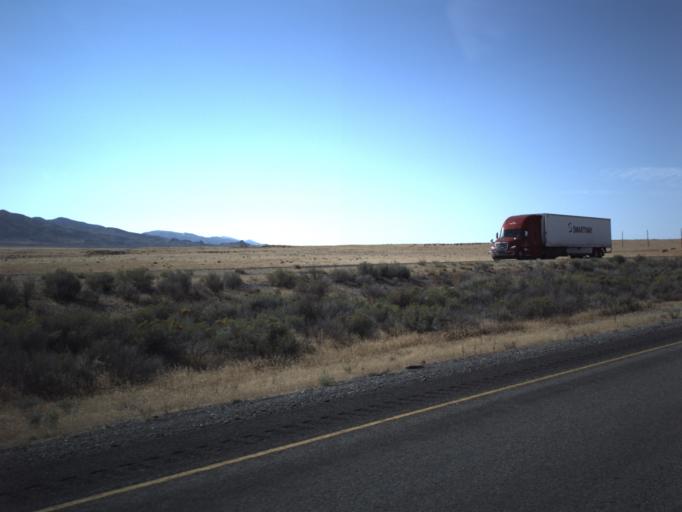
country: US
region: Utah
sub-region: Tooele County
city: Grantsville
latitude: 40.7785
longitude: -112.9710
